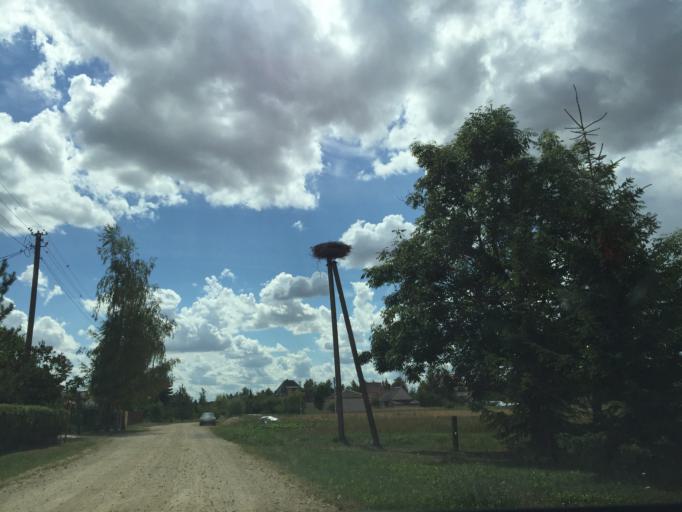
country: LV
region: Rundales
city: Pilsrundale
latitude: 56.2962
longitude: 23.8226
